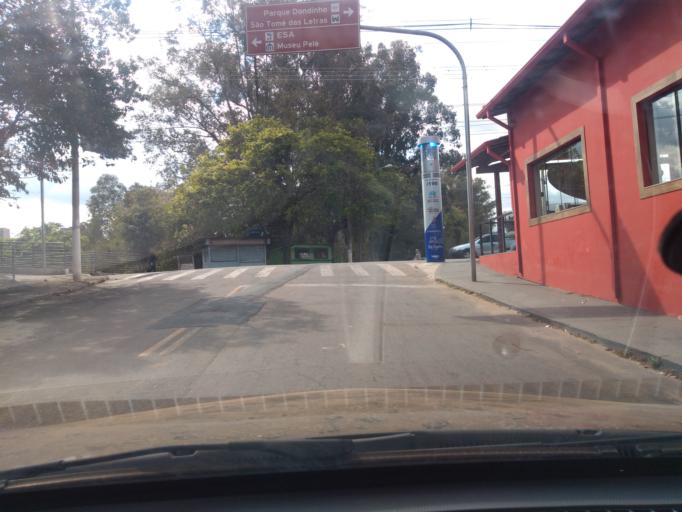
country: BR
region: Minas Gerais
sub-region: Tres Coracoes
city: Tres Coracoes
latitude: -21.7029
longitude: -45.2539
